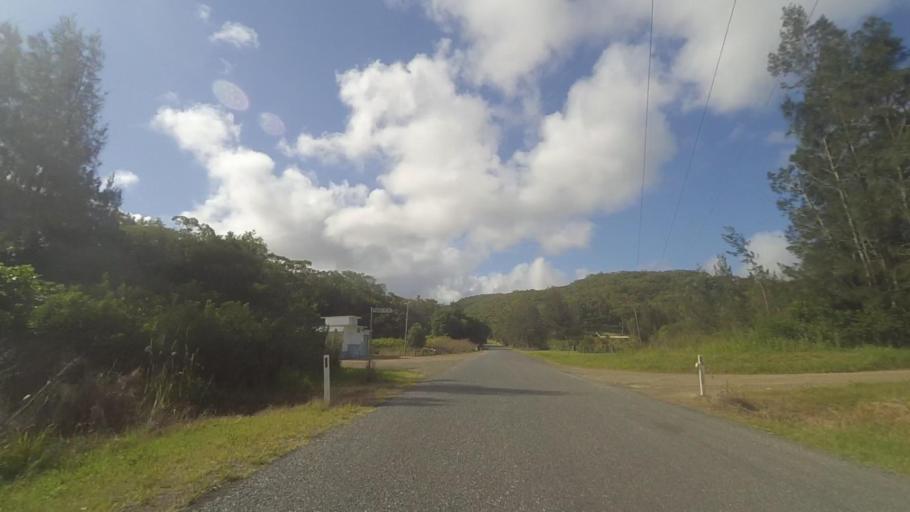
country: AU
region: New South Wales
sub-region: Great Lakes
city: Forster
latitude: -32.4009
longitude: 152.4602
